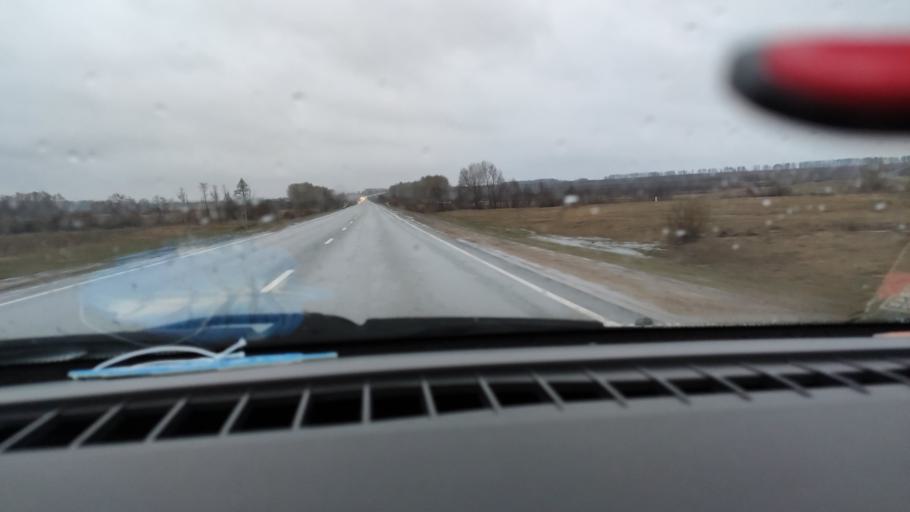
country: RU
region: Tatarstan
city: Mendeleyevsk
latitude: 55.9681
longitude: 52.3170
